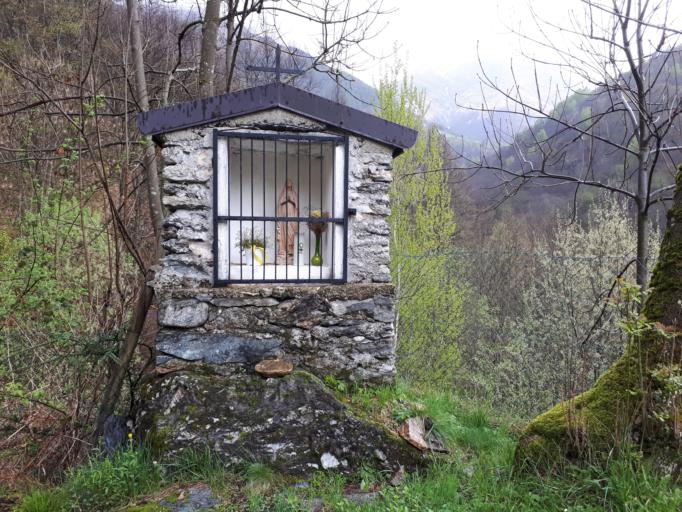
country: IT
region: Lombardy
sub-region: Provincia di Como
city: Garzeno
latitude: 46.1654
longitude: 9.2391
